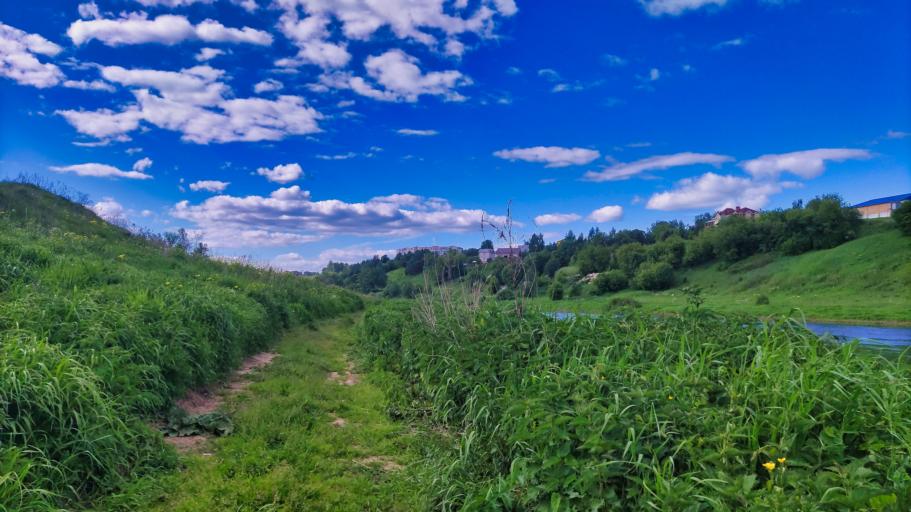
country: RU
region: Tverskaya
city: Rzhev
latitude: 56.2495
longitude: 34.3489
